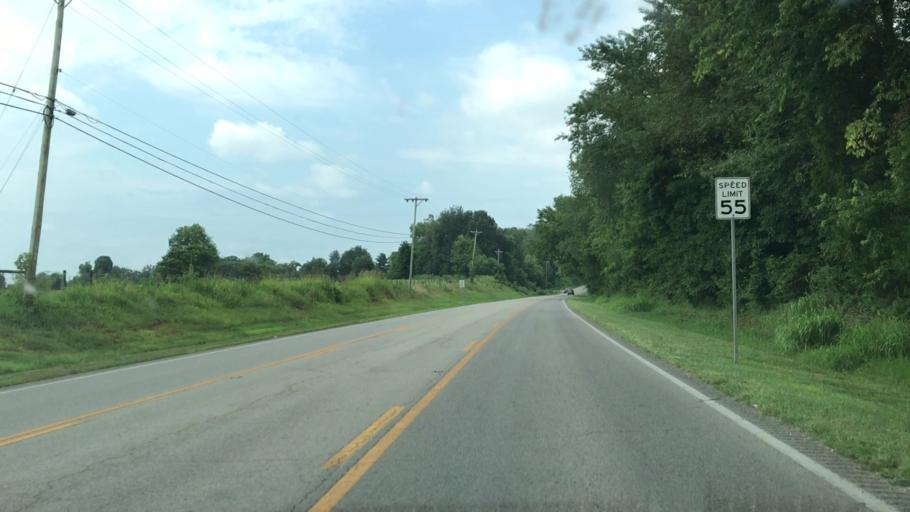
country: US
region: Kentucky
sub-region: Hart County
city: Horse Cave
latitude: 37.1594
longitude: -85.9242
